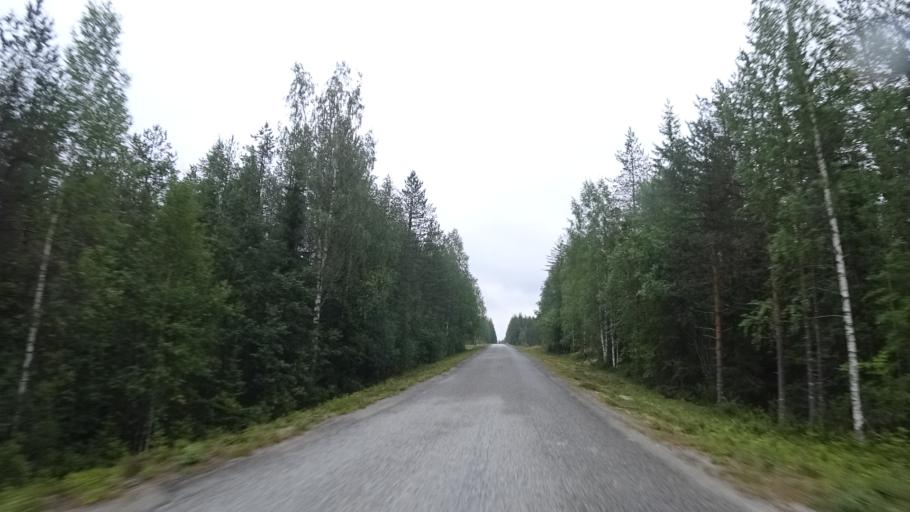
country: FI
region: North Karelia
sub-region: Joensuu
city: Ilomantsi
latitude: 63.2290
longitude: 30.8109
